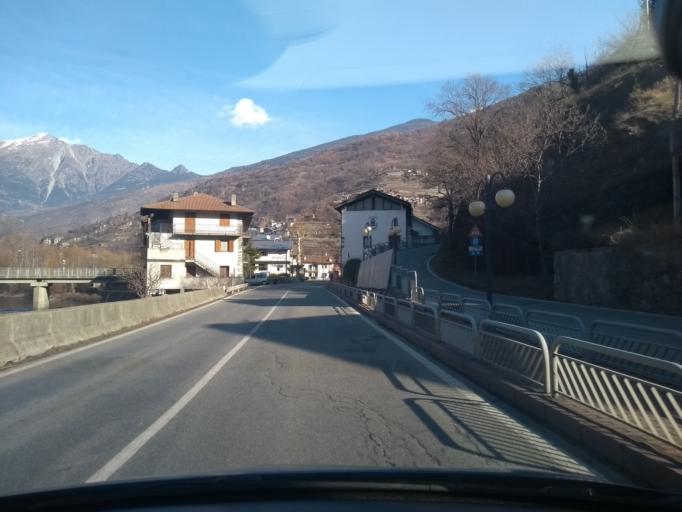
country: IT
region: Aosta Valley
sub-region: Valle d'Aosta
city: Montjovet
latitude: 45.7034
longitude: 7.6735
